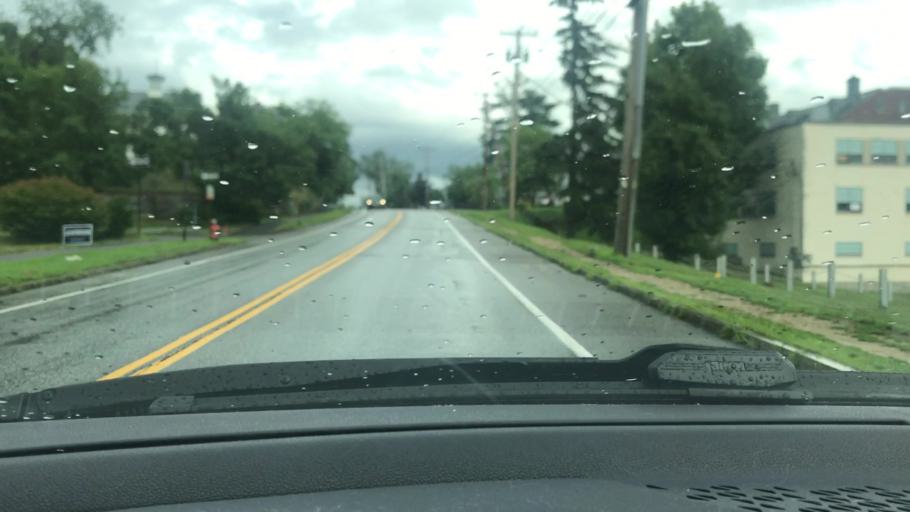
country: US
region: New Hampshire
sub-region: Merrimack County
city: Concord
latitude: 43.1996
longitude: -71.5479
